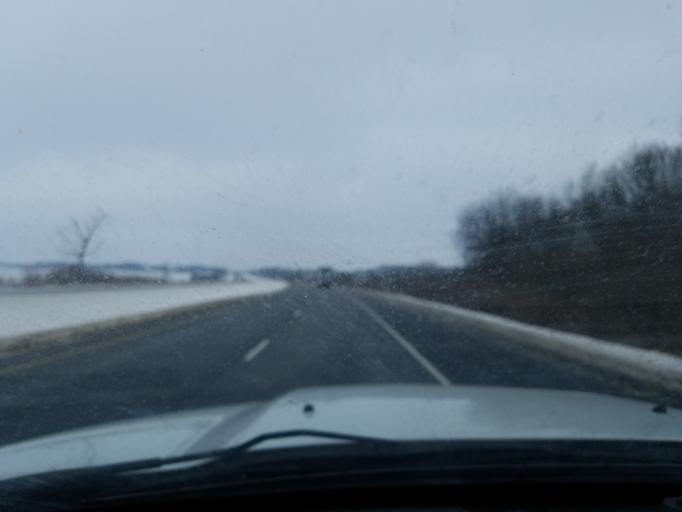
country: US
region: Indiana
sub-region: Marshall County
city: Argos
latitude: 41.2541
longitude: -86.2616
